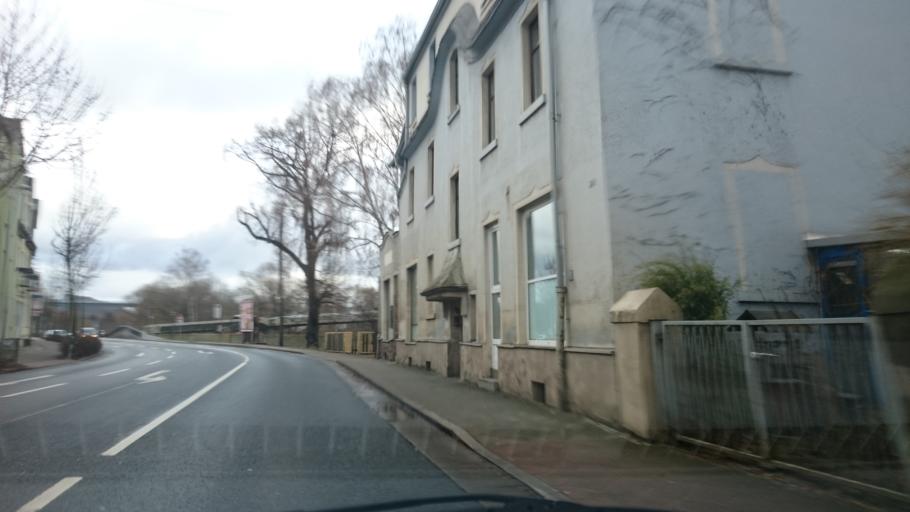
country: DE
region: Saxony
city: Wilkau-Hasslau
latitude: 50.6766
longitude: 12.5139
